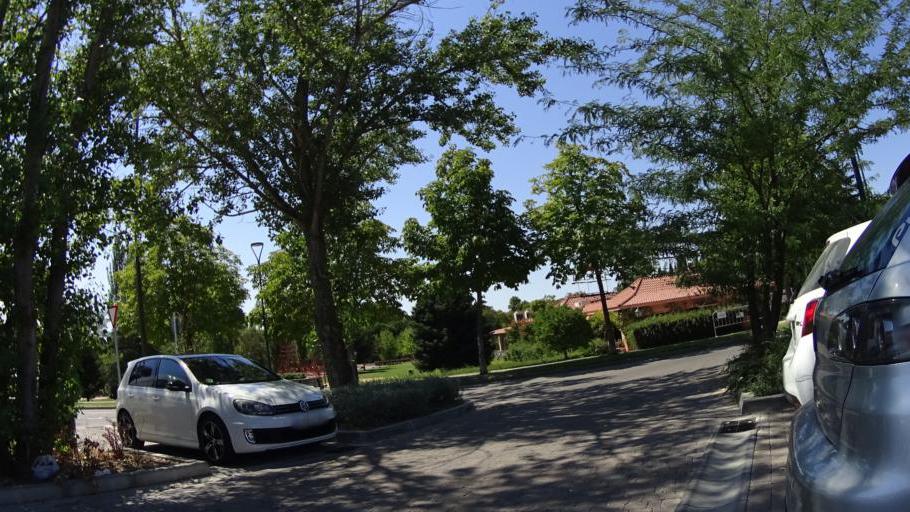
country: ES
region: Madrid
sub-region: Provincia de Madrid
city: Boadilla del Monte
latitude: 40.4028
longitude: -3.8761
